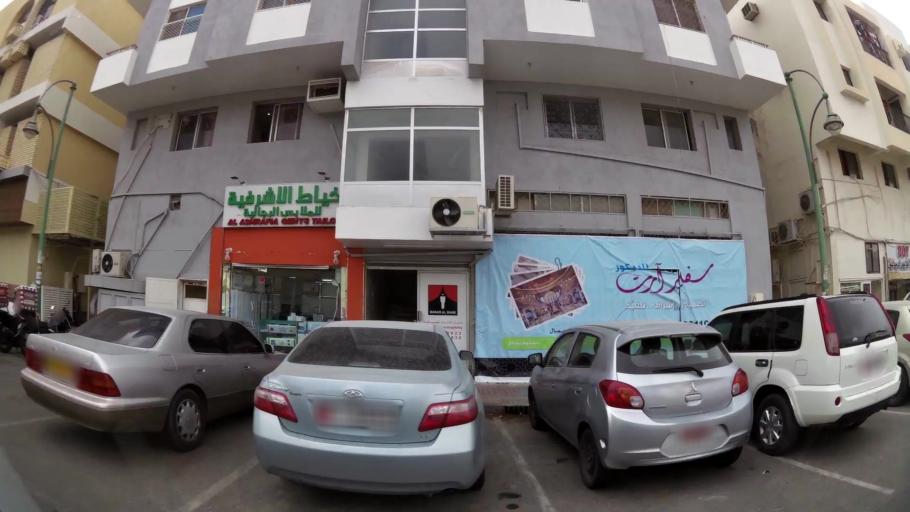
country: AE
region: Abu Dhabi
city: Al Ain
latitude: 24.2261
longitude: 55.7643
